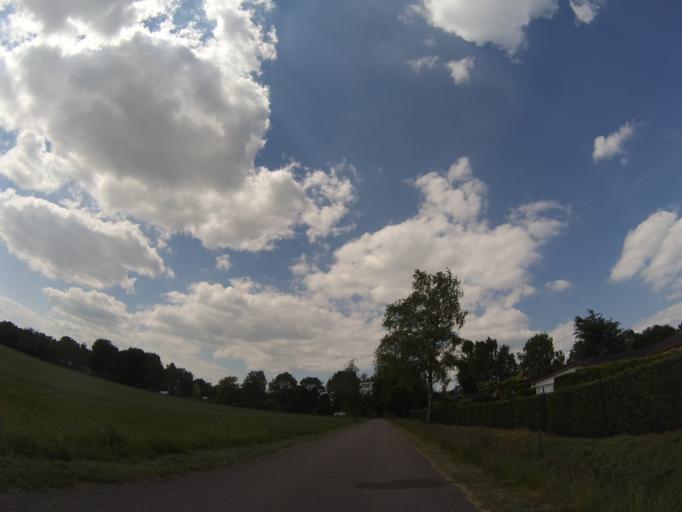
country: NL
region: Gelderland
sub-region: Gemeente Barneveld
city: Stroe
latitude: 52.1912
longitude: 5.6535
